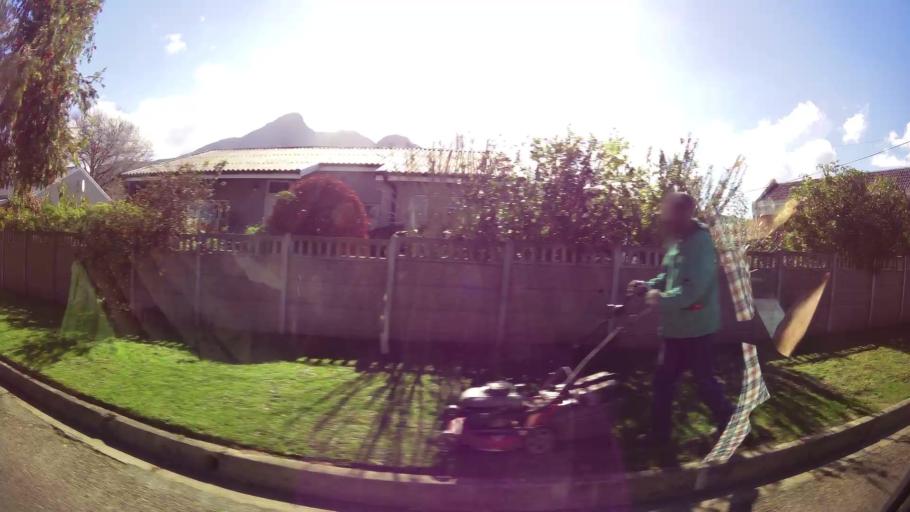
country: ZA
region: Western Cape
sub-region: Eden District Municipality
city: George
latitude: -33.9443
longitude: 22.4741
